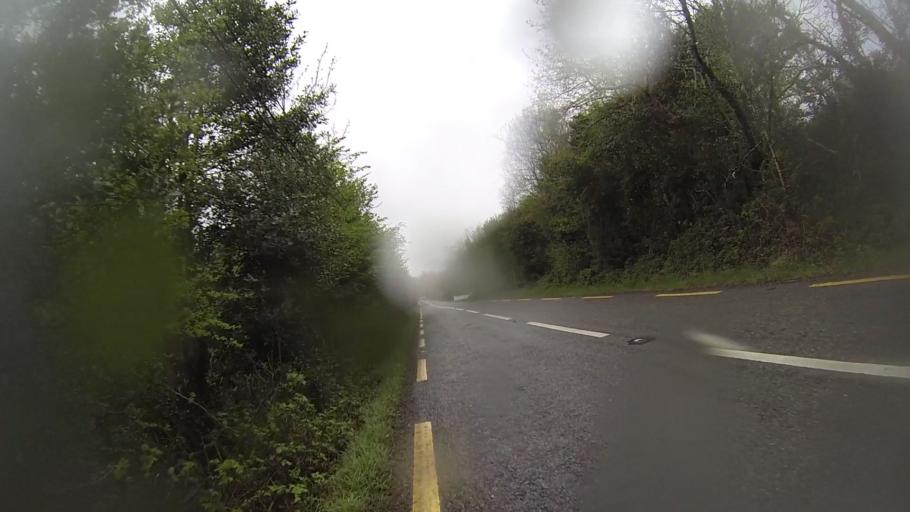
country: IE
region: Munster
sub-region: Ciarrai
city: Kenmare
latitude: 51.8201
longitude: -9.5300
